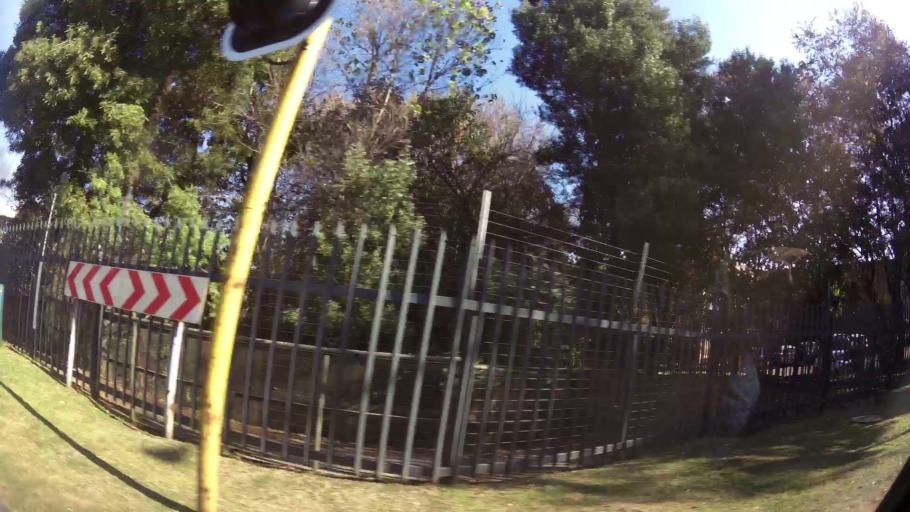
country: ZA
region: Gauteng
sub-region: Ekurhuleni Metropolitan Municipality
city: Germiston
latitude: -26.1712
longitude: 28.1351
